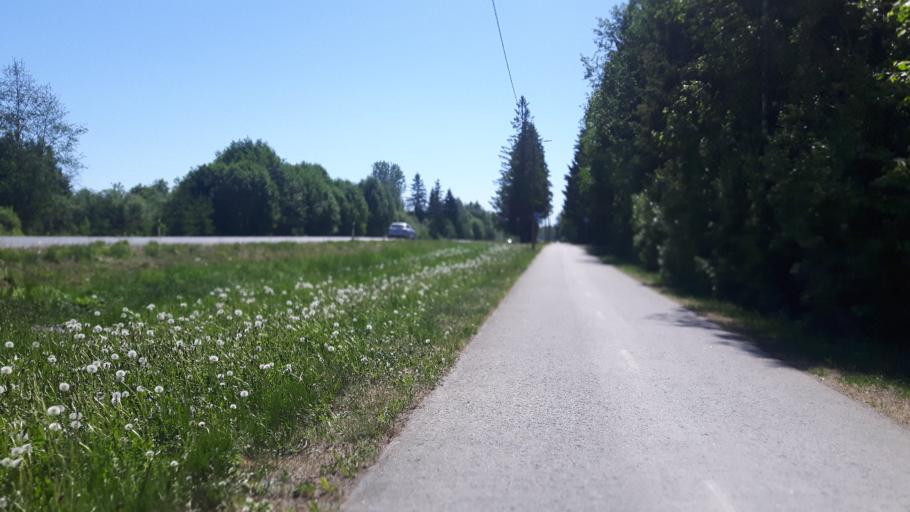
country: EE
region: Harju
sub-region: Saku vald
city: Saku
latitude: 59.2854
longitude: 24.6629
